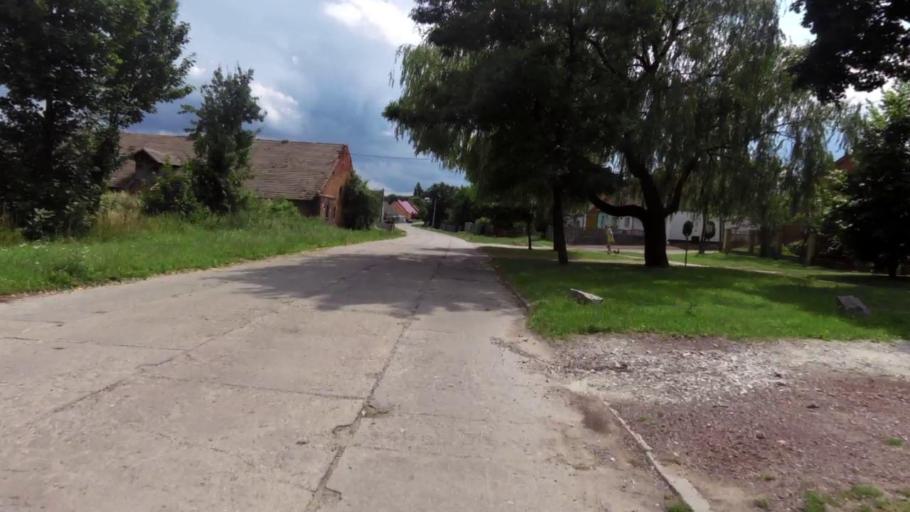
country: PL
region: West Pomeranian Voivodeship
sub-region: Powiat mysliborski
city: Nowogrodek Pomorski
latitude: 52.9907
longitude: 15.0581
